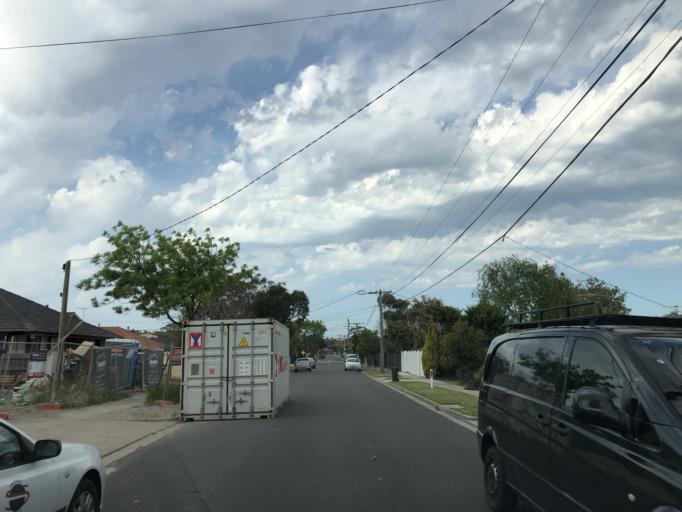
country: AU
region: Victoria
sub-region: Kingston
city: Carrum
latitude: -38.0868
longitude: 145.1308
